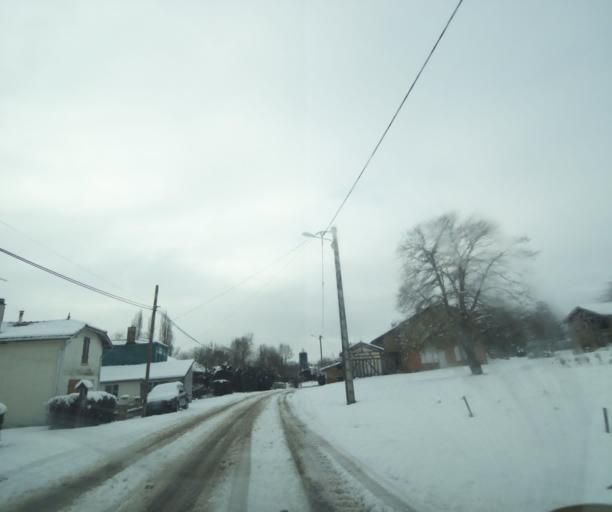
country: FR
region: Champagne-Ardenne
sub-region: Departement de la Haute-Marne
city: Montier-en-Der
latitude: 48.5181
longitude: 4.7005
